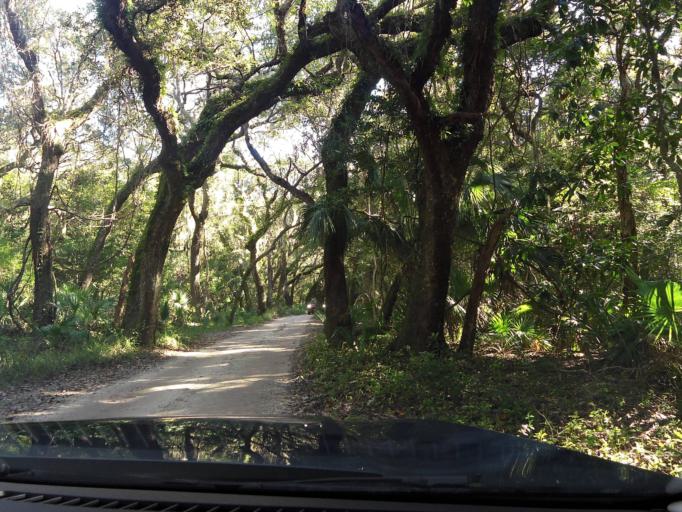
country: US
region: Florida
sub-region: Duval County
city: Atlantic Beach
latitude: 30.4345
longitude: -81.4301
